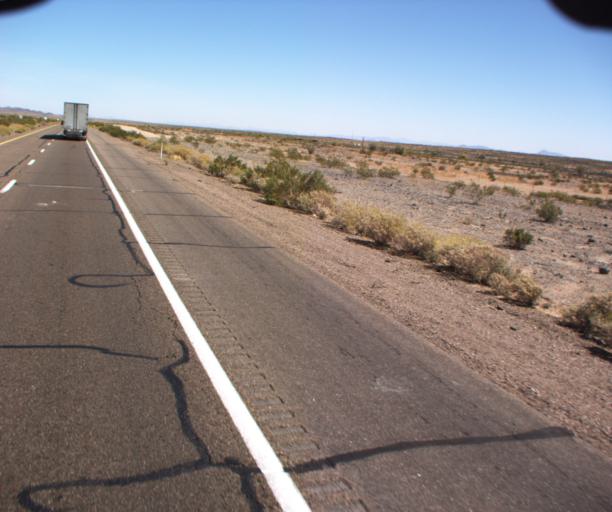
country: US
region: Arizona
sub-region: Maricopa County
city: Gila Bend
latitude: 32.8717
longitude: -113.1346
